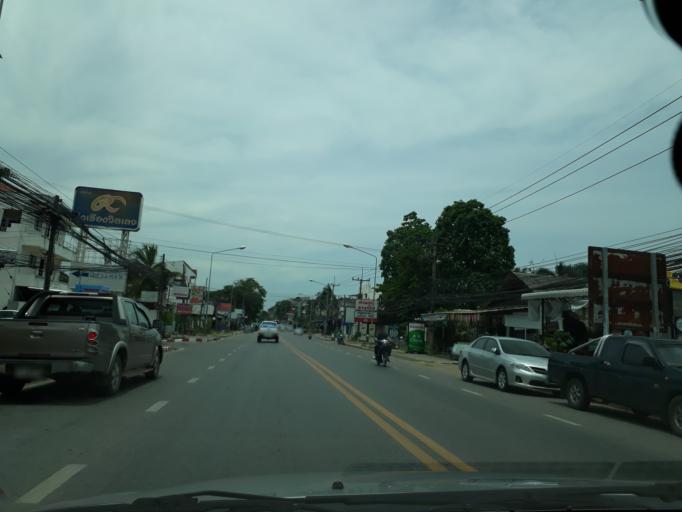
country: TH
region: Khon Kaen
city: Khon Kaen
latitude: 16.4350
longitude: 102.8553
